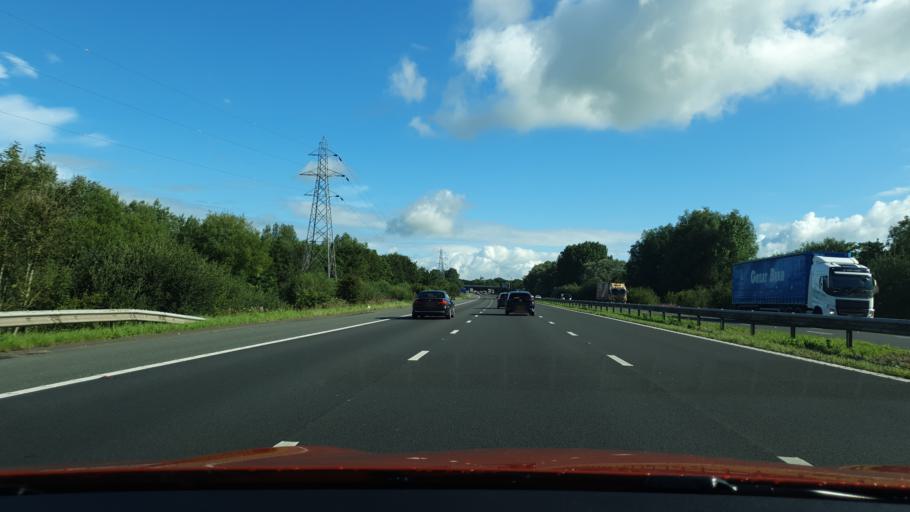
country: GB
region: England
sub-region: Lancashire
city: Carnforth
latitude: 54.1439
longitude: -2.7401
